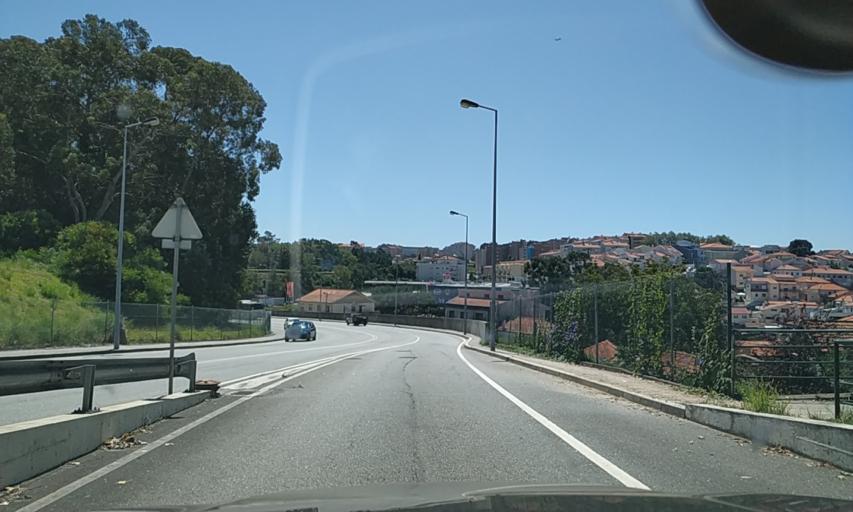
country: PT
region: Porto
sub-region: Vila Nova de Gaia
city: Canidelo
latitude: 41.1412
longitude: -8.6420
